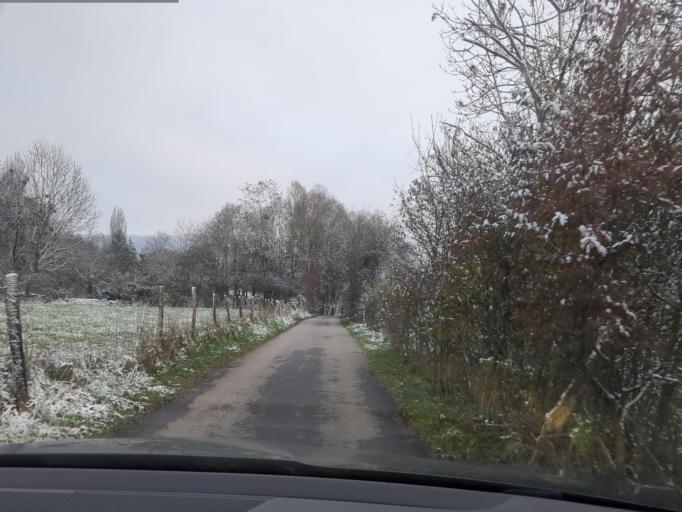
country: FR
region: Franche-Comte
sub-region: Departement du Jura
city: Perrigny
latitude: 46.6630
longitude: 5.5829
